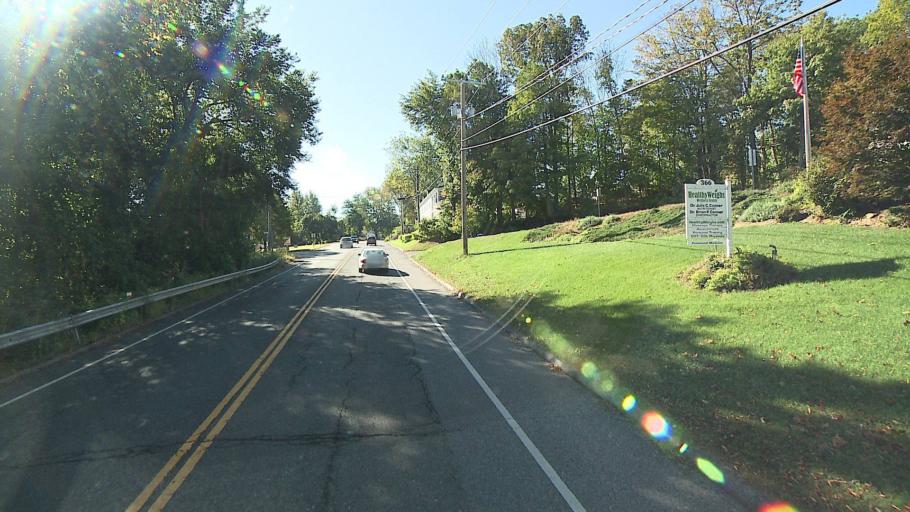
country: US
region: Connecticut
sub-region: Fairfield County
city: Danbury
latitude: 41.4534
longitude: -73.4025
